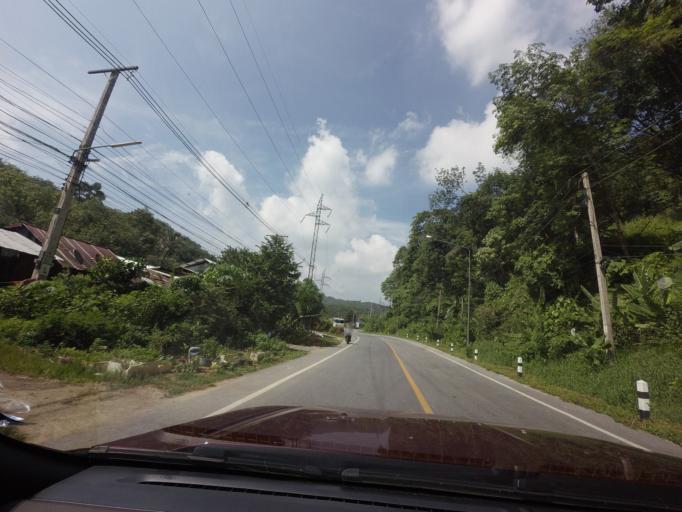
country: TH
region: Yala
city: Betong
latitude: 5.8276
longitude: 101.1122
